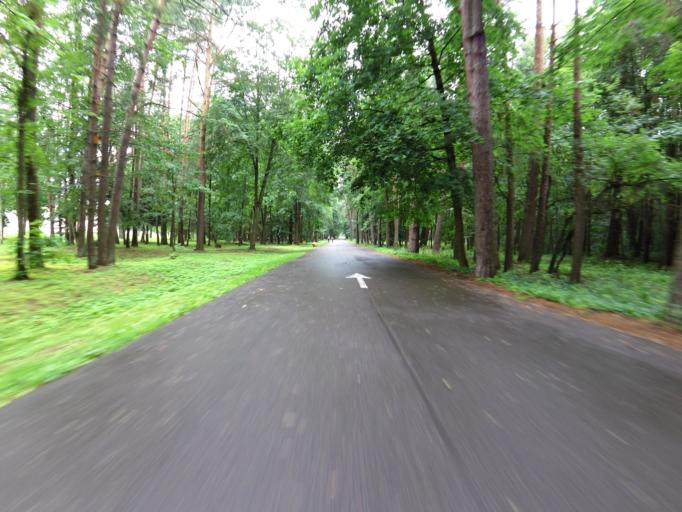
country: LT
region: Vilnius County
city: Vilkpede
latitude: 54.6841
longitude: 25.2394
